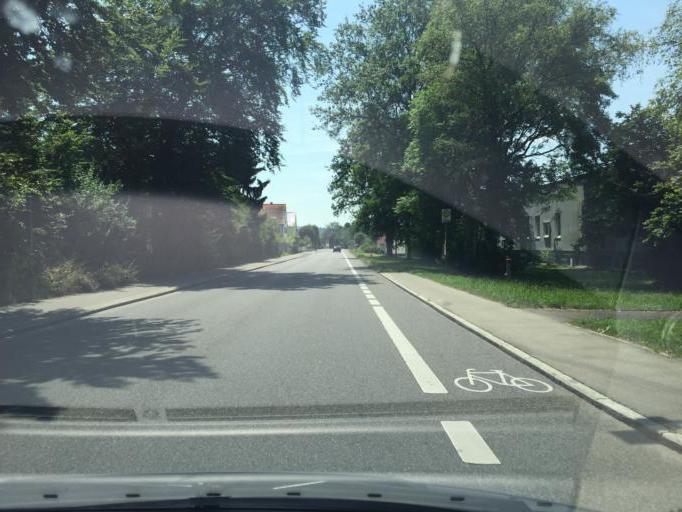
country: DE
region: Baden-Wuerttemberg
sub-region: Freiburg Region
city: Rielasingen-Worblingen
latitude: 47.7395
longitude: 8.8412
